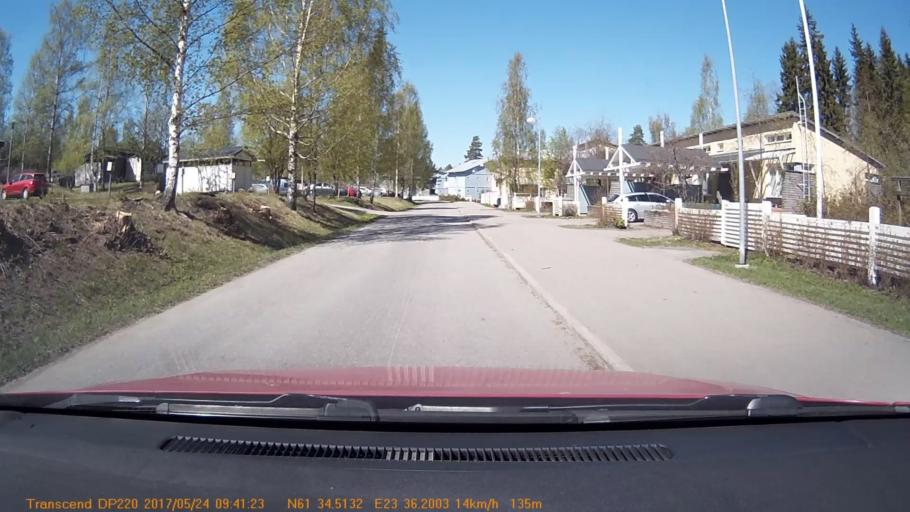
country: FI
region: Pirkanmaa
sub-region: Tampere
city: Yloejaervi
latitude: 61.5749
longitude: 23.6027
